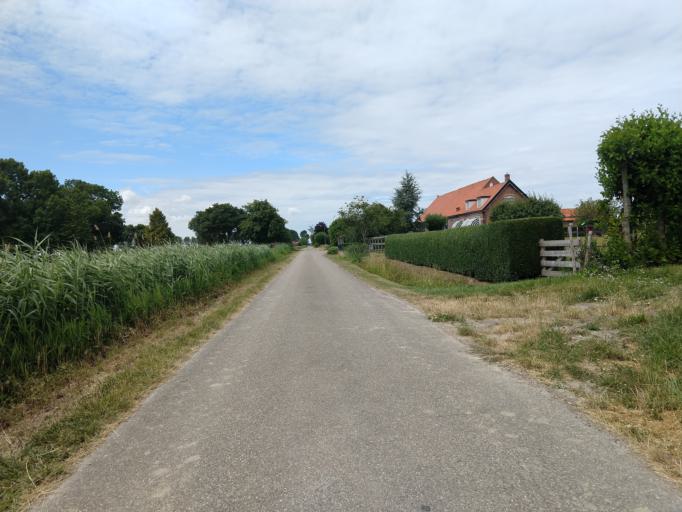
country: NL
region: Zeeland
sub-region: Gemeente Noord-Beveland
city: Kamperland
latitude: 51.5325
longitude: 3.7941
